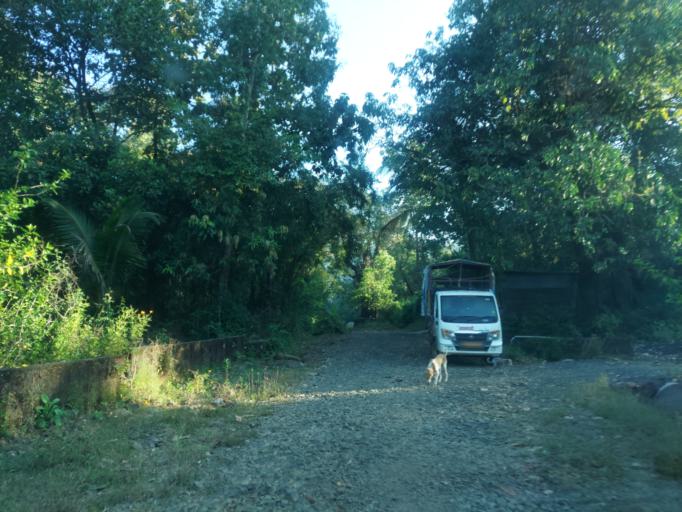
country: IN
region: Maharashtra
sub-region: Sindhudurg
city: Kudal
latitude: 16.0695
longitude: 73.8240
